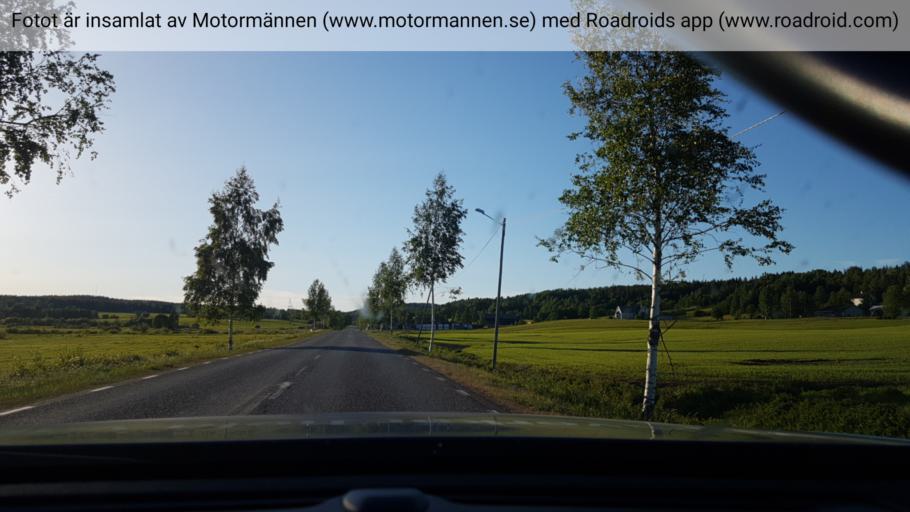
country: SE
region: Vaesterbotten
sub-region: Vannas Kommun
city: Vaennaes
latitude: 63.7540
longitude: 19.6380
